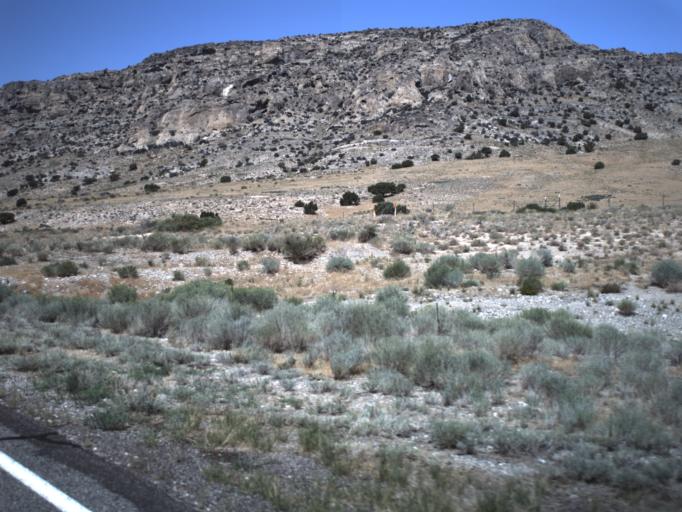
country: US
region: Utah
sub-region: Beaver County
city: Milford
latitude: 39.0726
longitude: -113.6461
